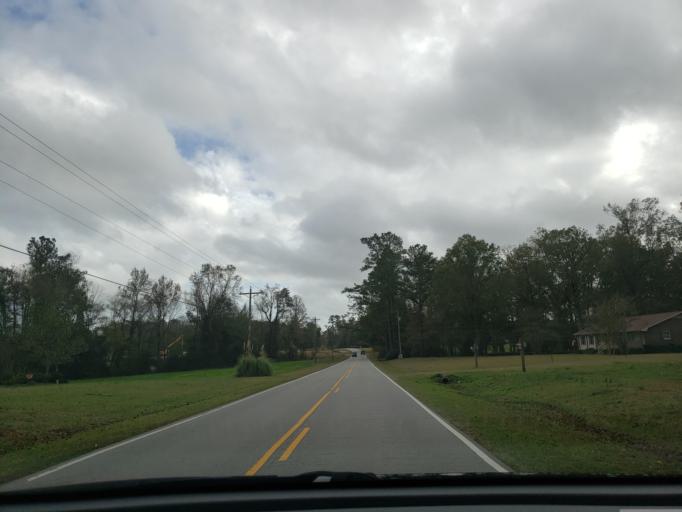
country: US
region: North Carolina
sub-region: Onslow County
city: Jacksonville
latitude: 34.7287
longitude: -77.5822
